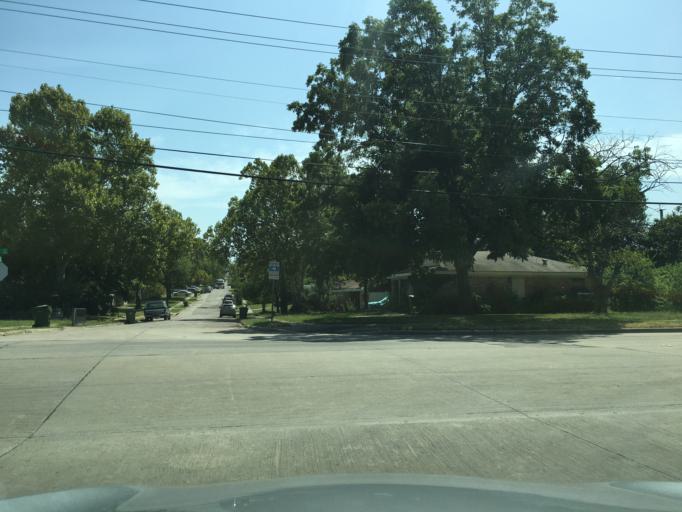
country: US
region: Texas
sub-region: Dallas County
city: Garland
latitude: 32.8906
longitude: -96.6224
